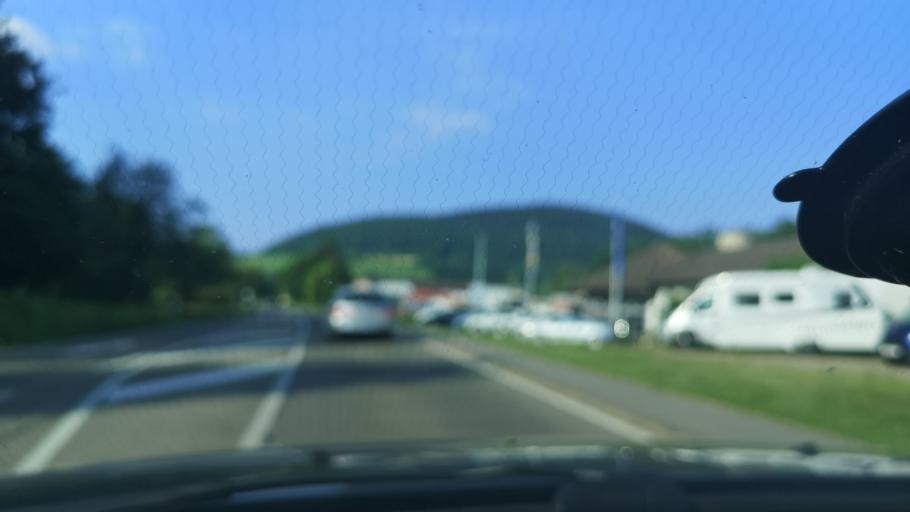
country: DE
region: Baden-Wuerttemberg
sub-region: Regierungsbezirk Stuttgart
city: Deggingen
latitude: 48.6025
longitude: 9.7297
